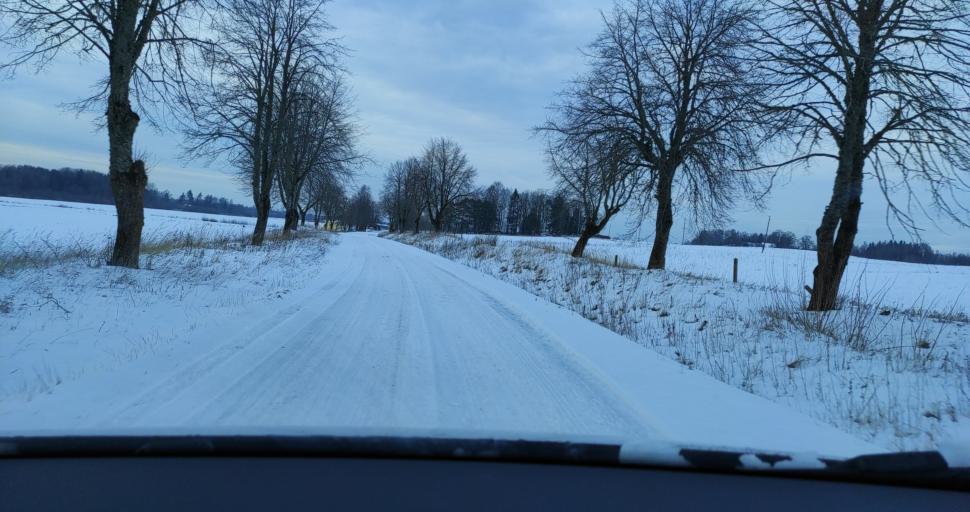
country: LV
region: Kuldigas Rajons
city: Kuldiga
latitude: 56.9464
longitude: 22.0244
